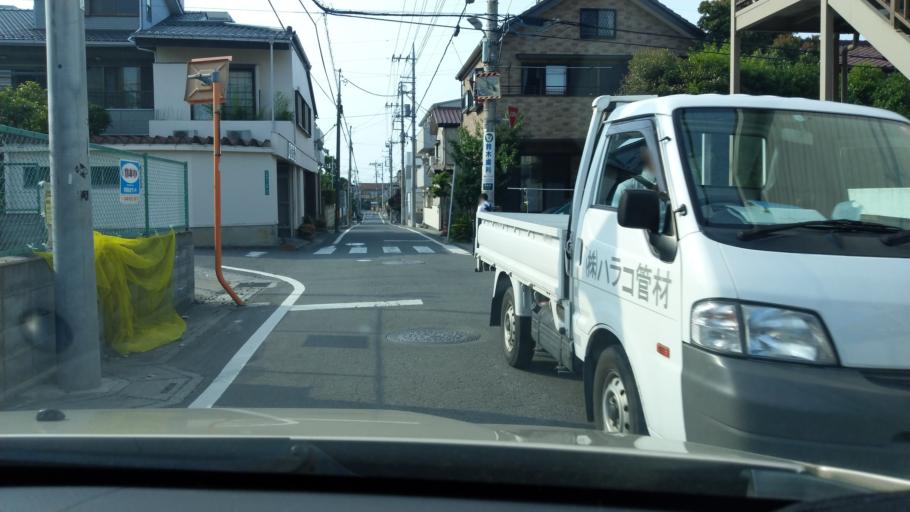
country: JP
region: Saitama
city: Yono
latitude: 35.8920
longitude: 139.6192
